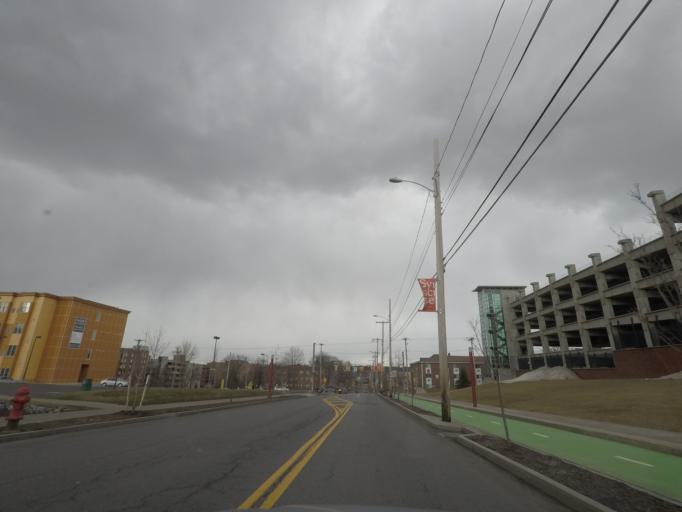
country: US
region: New York
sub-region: Onondaga County
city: Syracuse
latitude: 43.0434
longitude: -76.1344
